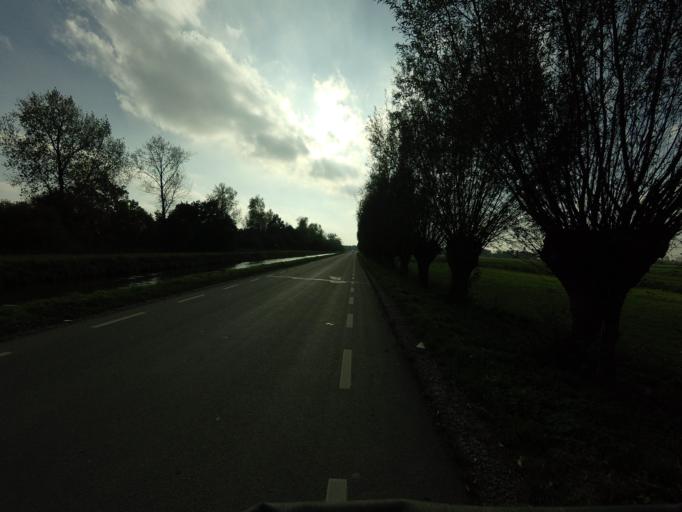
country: NL
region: Gelderland
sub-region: Gemeente Culemborg
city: Culemborg
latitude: 51.9341
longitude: 5.2529
